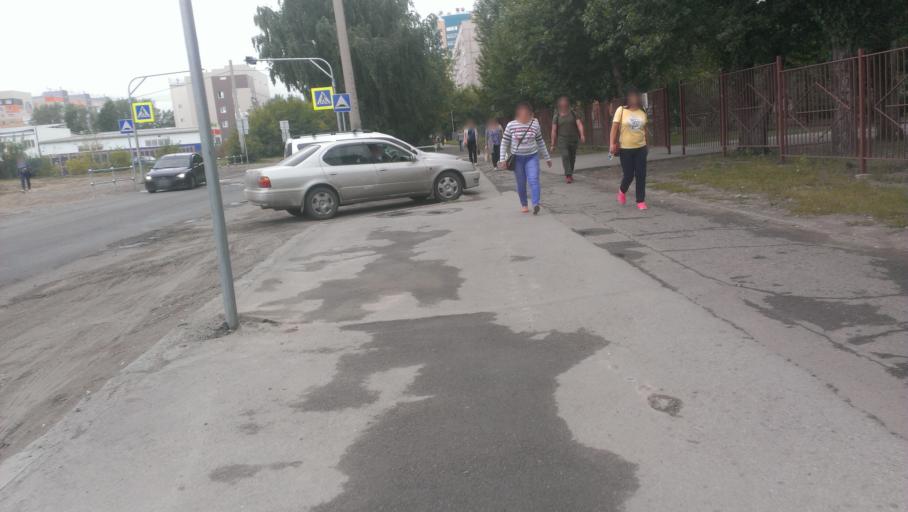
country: RU
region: Altai Krai
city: Novosilikatnyy
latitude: 53.3400
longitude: 83.6659
